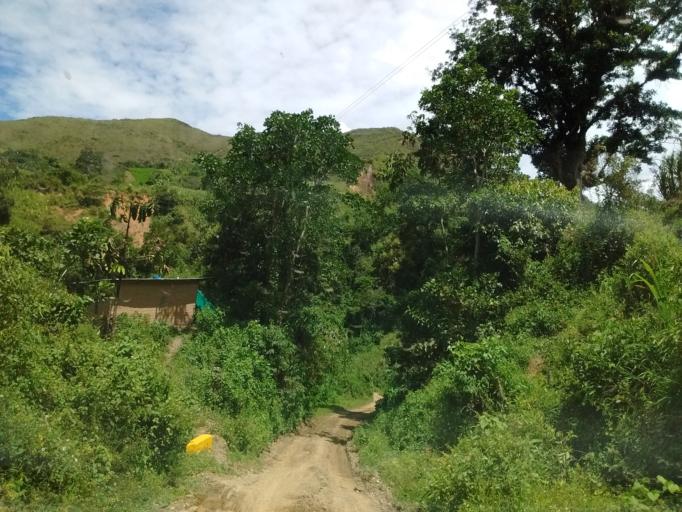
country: CO
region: Cauca
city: Villa Rica
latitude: 2.6629
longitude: -76.7673
